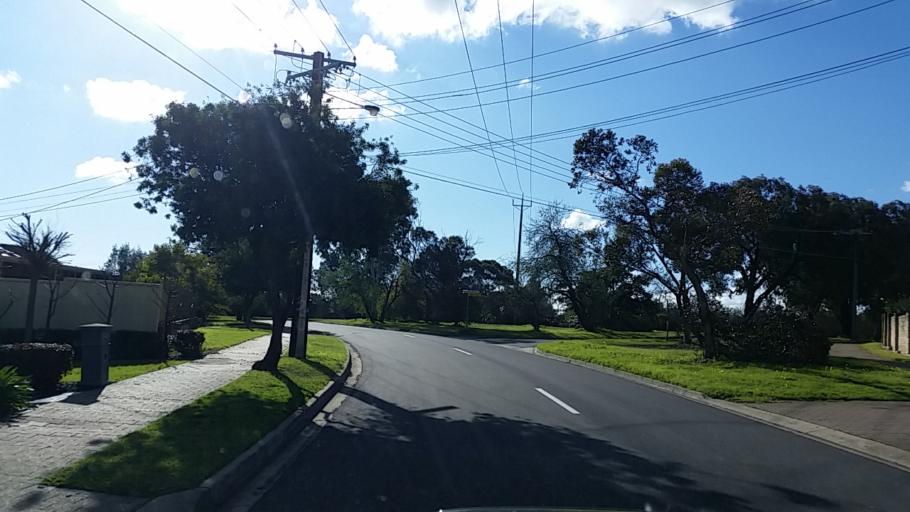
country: AU
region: South Australia
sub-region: Tea Tree Gully
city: Modbury
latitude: -34.8496
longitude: 138.6748
